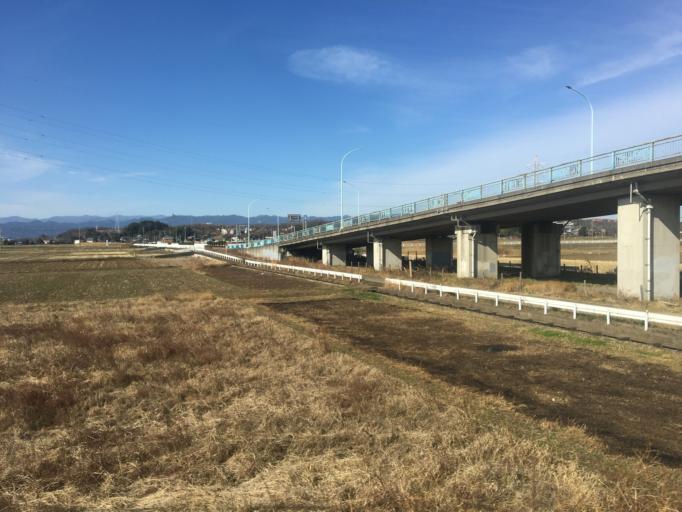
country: JP
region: Saitama
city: Sakado
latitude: 35.9907
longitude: 139.4005
